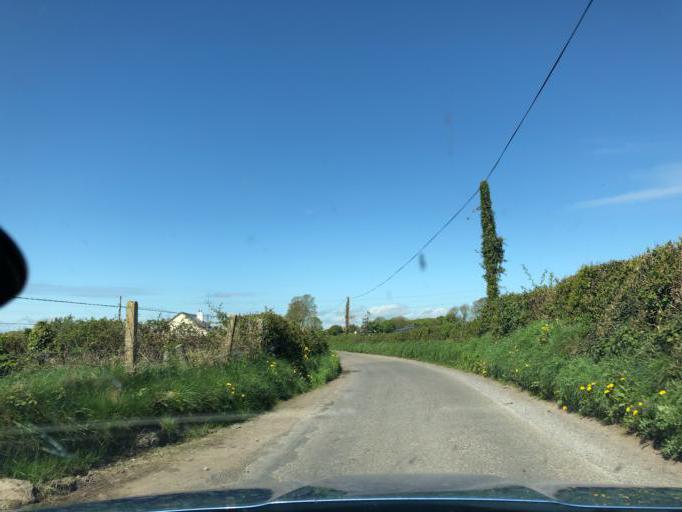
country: IE
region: Connaught
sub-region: County Galway
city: Portumna
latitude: 53.1572
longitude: -8.3209
